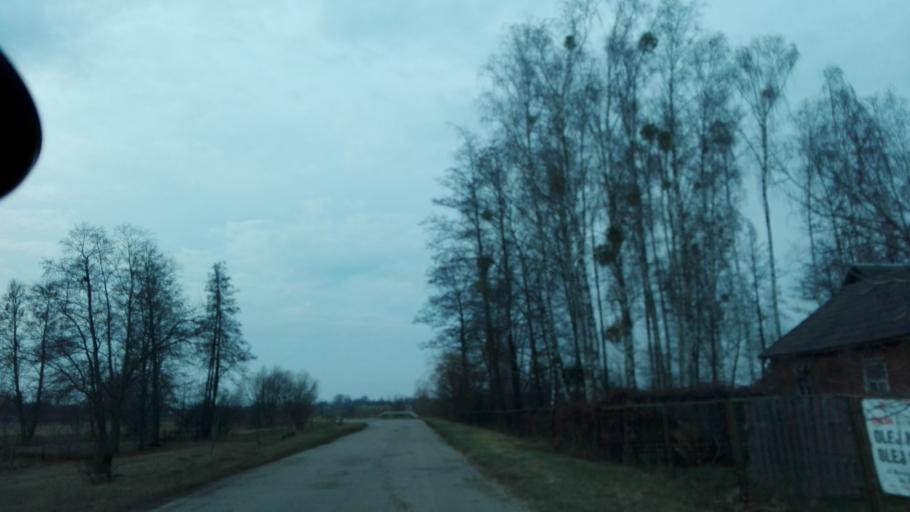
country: PL
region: Lublin Voivodeship
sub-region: Powiat bialski
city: Sosnowka
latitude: 51.7249
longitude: 23.4409
